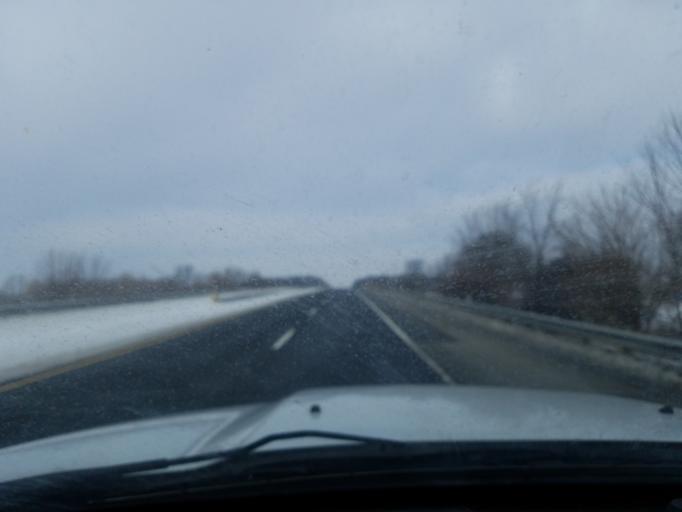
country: US
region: Indiana
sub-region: Marshall County
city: Plymouth
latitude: 41.3311
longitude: -86.2758
